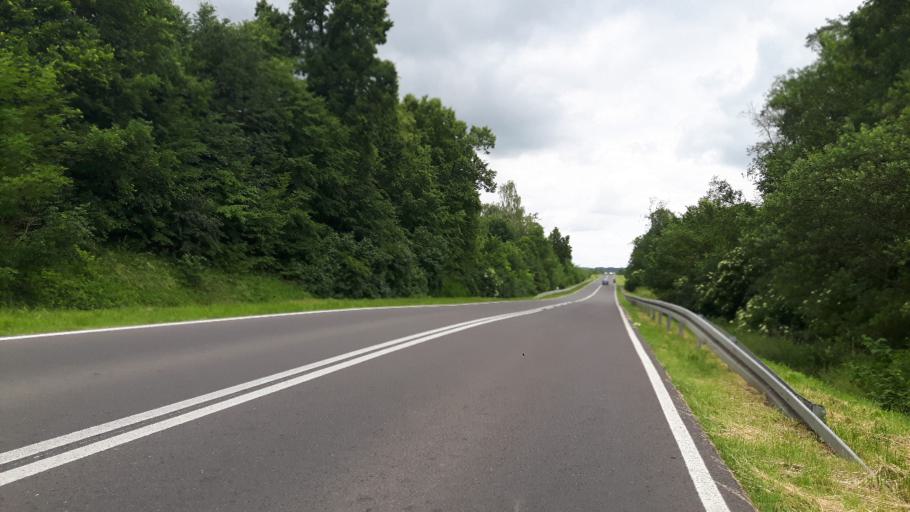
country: PL
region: West Pomeranian Voivodeship
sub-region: Powiat policki
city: Kolbaskowo
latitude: 53.3134
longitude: 14.4124
